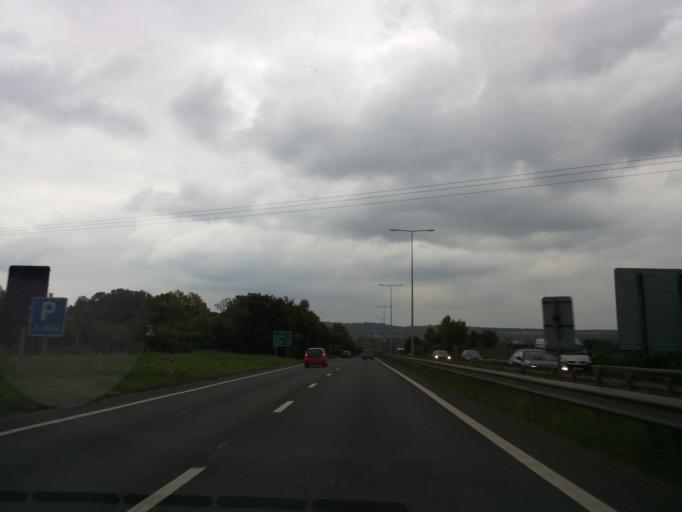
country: GB
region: England
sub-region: Kent
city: Faversham
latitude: 51.3006
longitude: 0.9303
